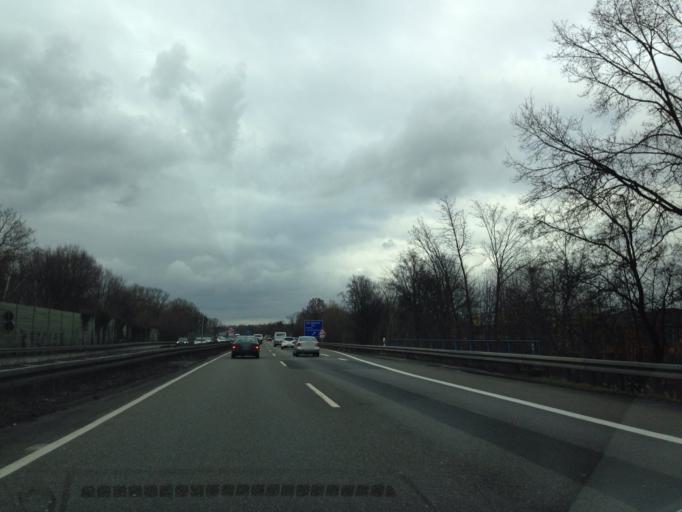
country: DE
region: North Rhine-Westphalia
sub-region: Regierungsbezirk Arnsberg
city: Herne
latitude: 51.5655
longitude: 7.1933
